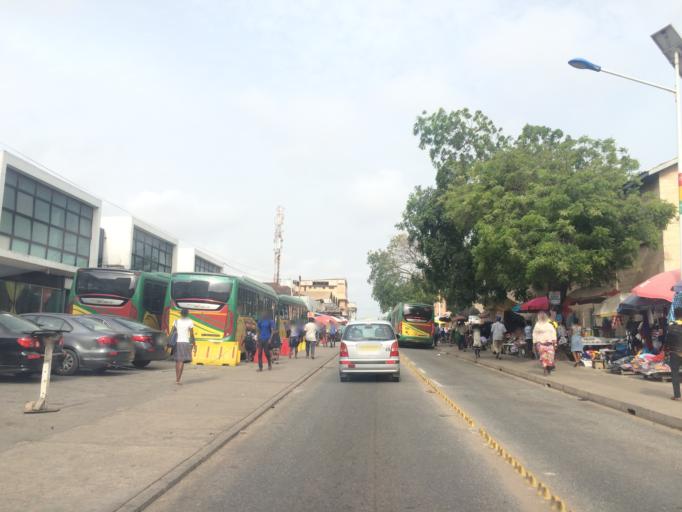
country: GH
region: Greater Accra
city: Accra
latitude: 5.5516
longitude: -0.2105
